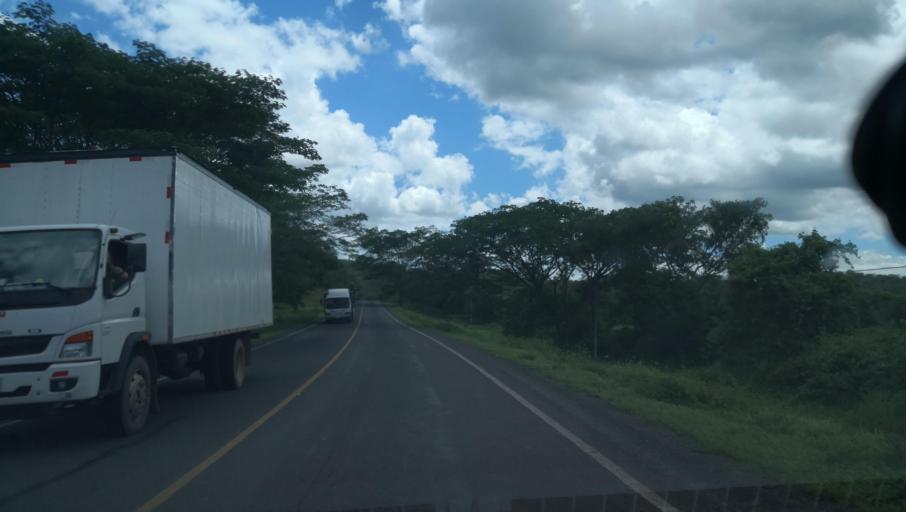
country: NI
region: Madriz
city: Palacaguina
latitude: 13.4344
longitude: -86.4161
